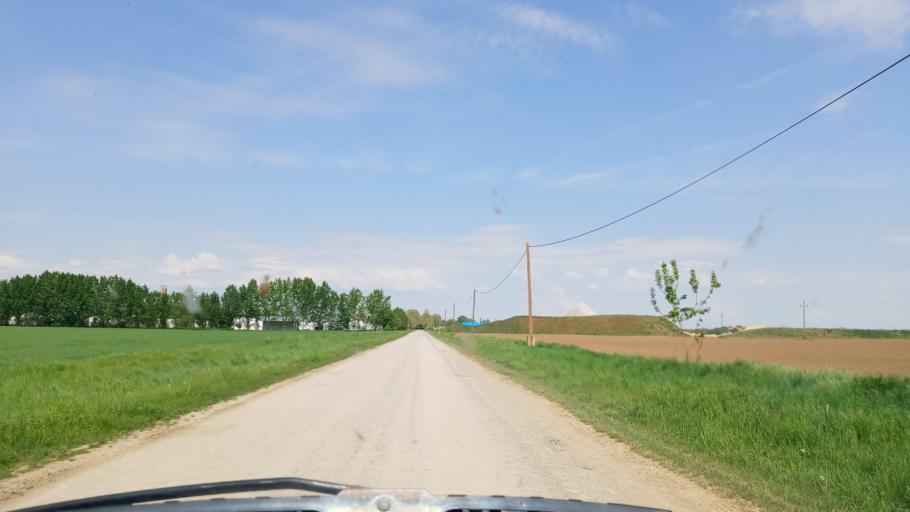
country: HU
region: Baranya
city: Boly
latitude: 45.9066
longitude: 18.5508
